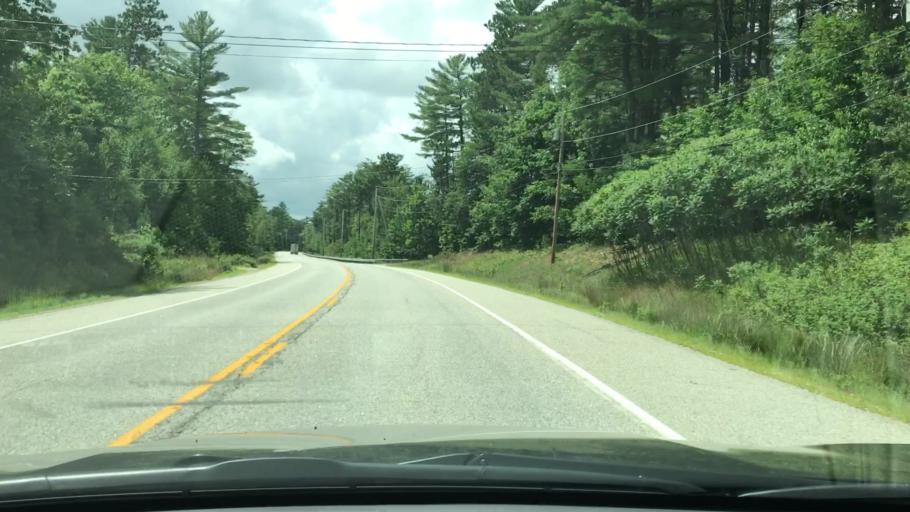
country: US
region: Maine
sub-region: Oxford County
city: Bethel
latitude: 44.3991
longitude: -70.6866
